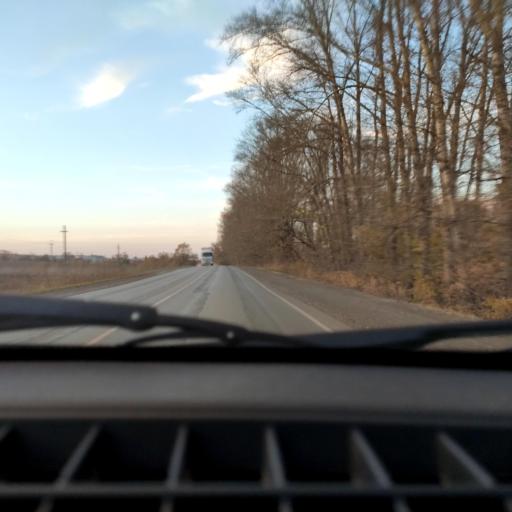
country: RU
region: Bashkortostan
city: Avdon
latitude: 54.7297
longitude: 55.8052
